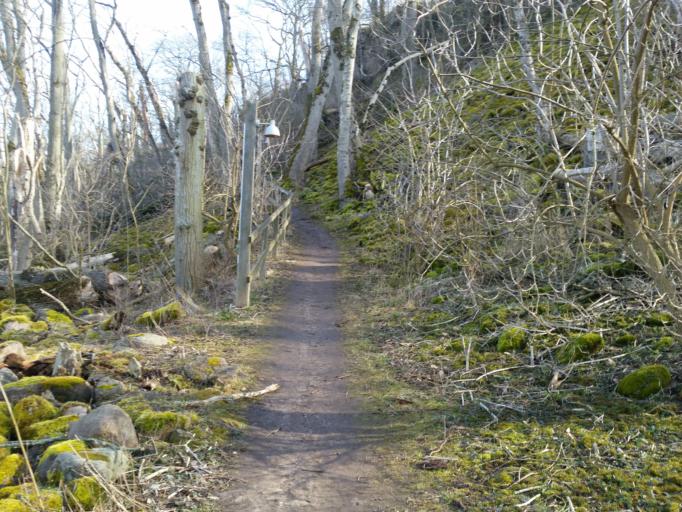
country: SE
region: Kalmar
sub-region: Borgholms Kommun
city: Borgholm
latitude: 56.8716
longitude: 16.6468
